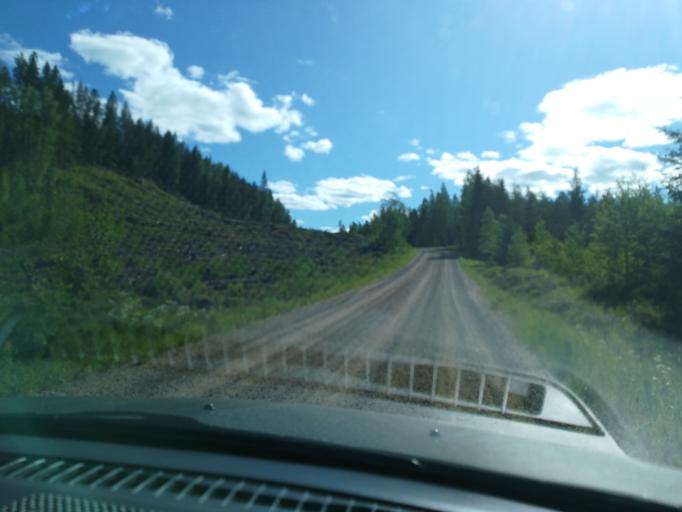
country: FI
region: Southern Savonia
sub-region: Mikkeli
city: Puumala
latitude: 61.6552
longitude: 28.1117
